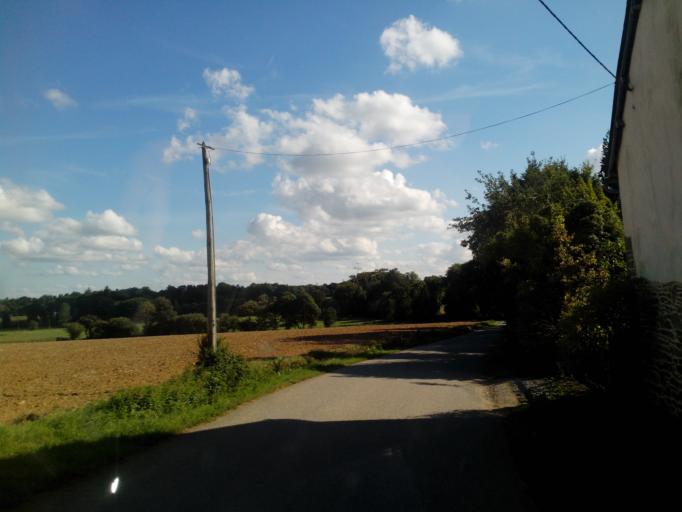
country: FR
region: Brittany
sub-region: Departement des Cotes-d'Armor
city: Merdrignac
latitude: 48.1417
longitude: -2.4017
